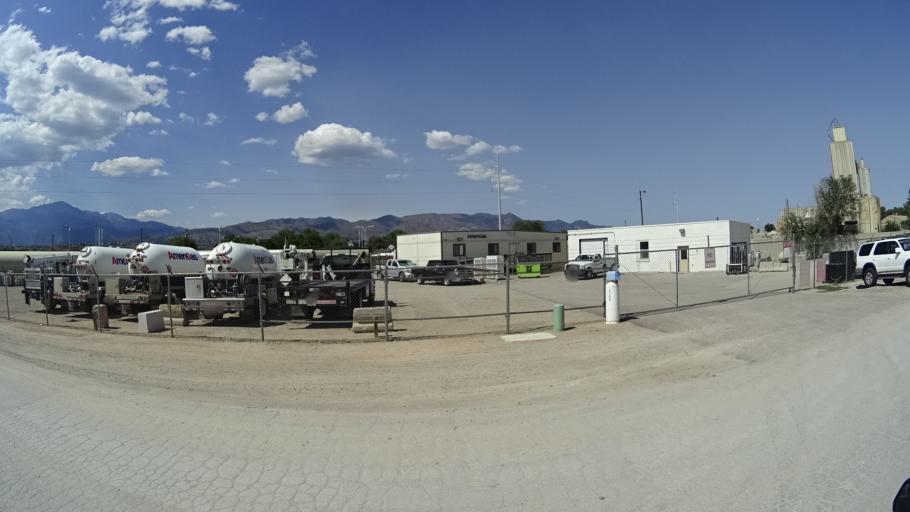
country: US
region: Colorado
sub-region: El Paso County
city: Colorado Springs
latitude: 38.8868
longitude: -104.8180
